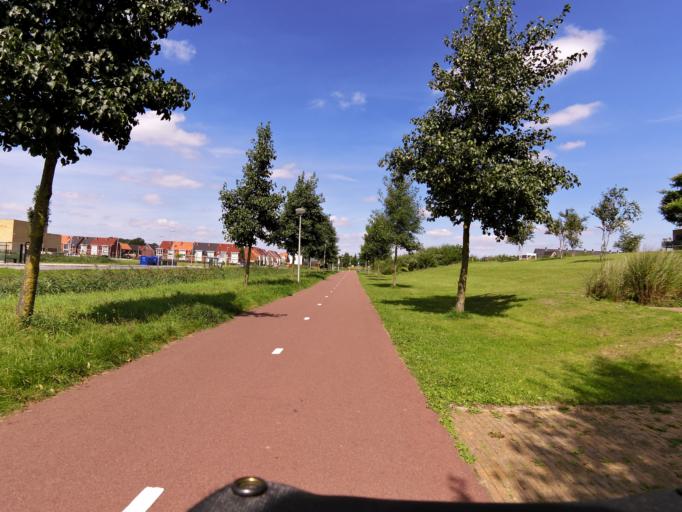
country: NL
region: South Holland
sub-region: Gemeente Barendrecht
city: Barendrecht
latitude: 51.8443
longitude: 4.5282
